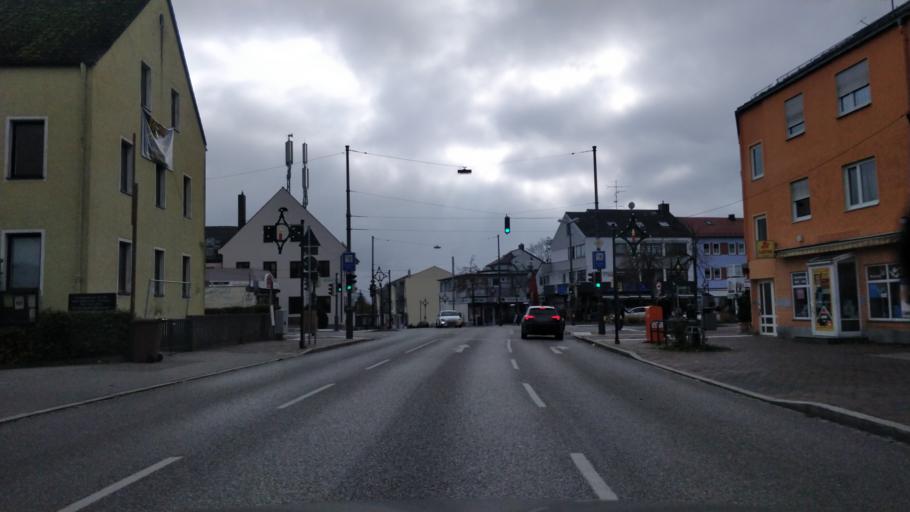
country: DE
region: Bavaria
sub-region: Swabia
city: Friedberg
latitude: 48.3562
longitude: 10.9842
